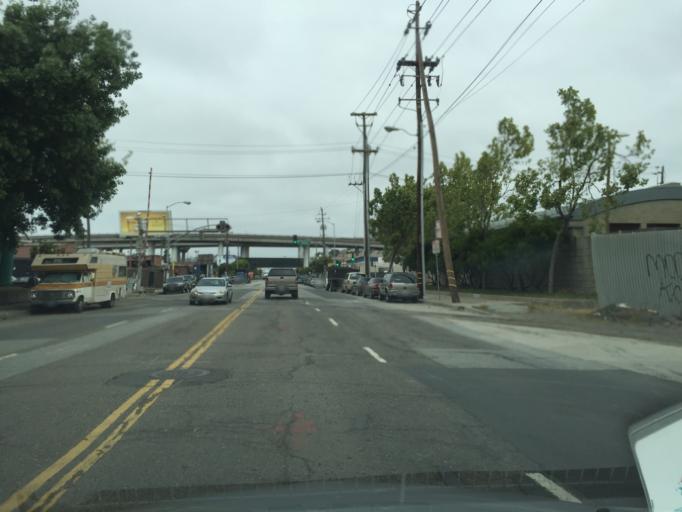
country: US
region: California
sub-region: San Francisco County
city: San Francisco
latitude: 37.7447
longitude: -122.3914
